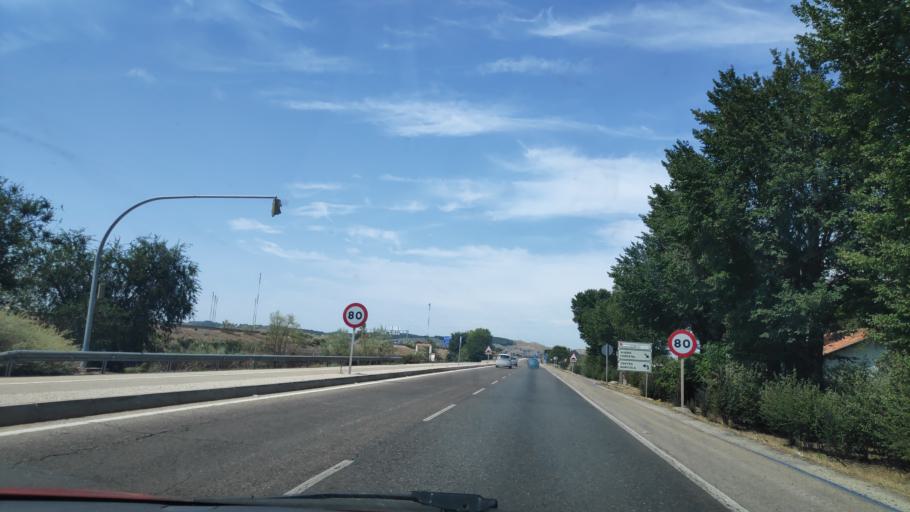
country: ES
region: Madrid
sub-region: Provincia de Madrid
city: Vaciamadrid
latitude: 40.3131
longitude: -3.4930
